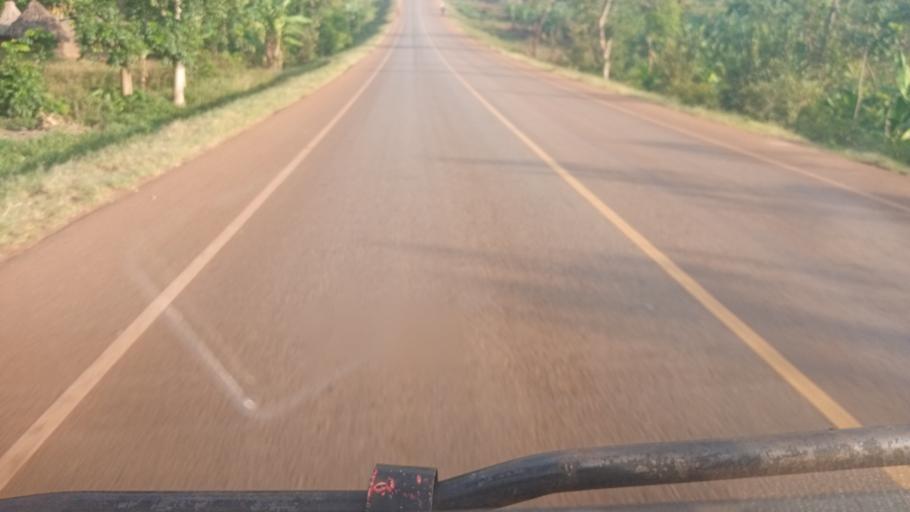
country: UG
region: Eastern Region
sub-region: Sironko District
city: Sironko
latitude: 1.3313
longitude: 34.3240
